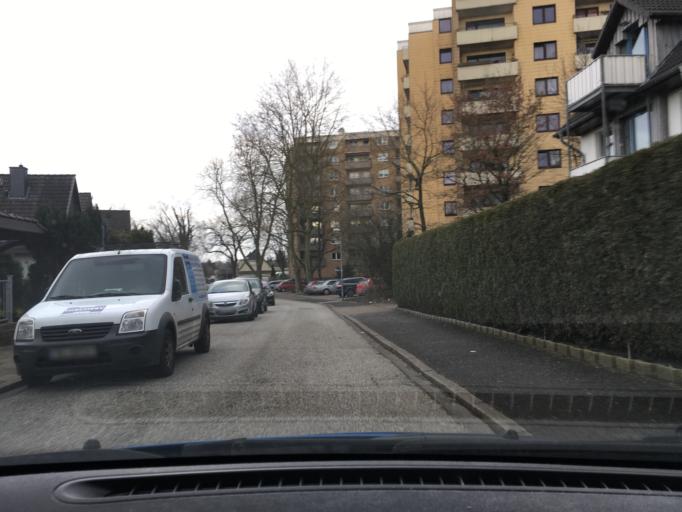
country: DE
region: Schleswig-Holstein
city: Wedel
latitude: 53.5753
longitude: 9.7178
